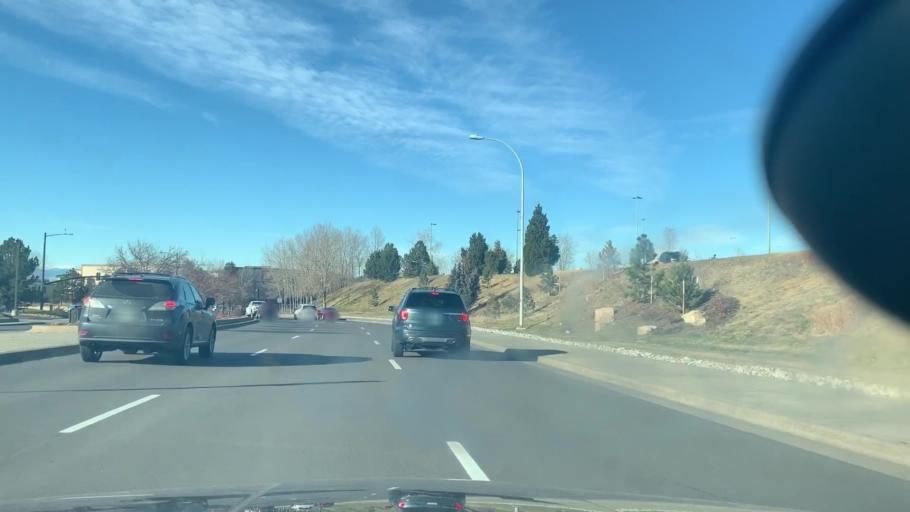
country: US
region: Colorado
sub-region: Adams County
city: Lone Tree
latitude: 39.5622
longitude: -104.8800
